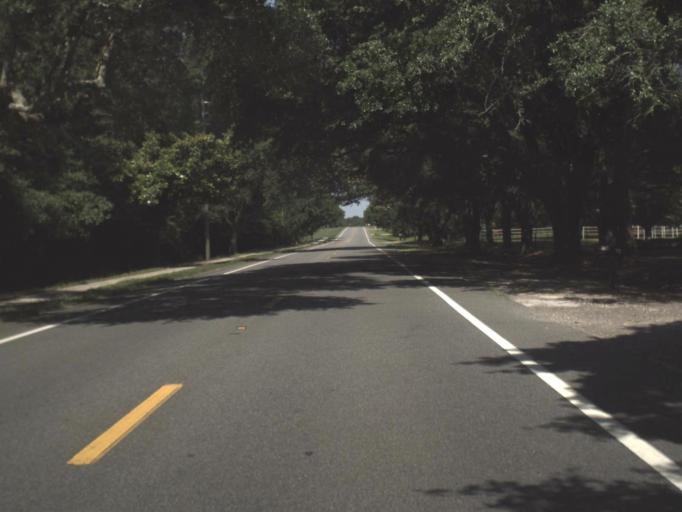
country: US
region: Florida
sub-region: Clay County
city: Asbury Lake
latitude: 29.9823
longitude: -81.8294
